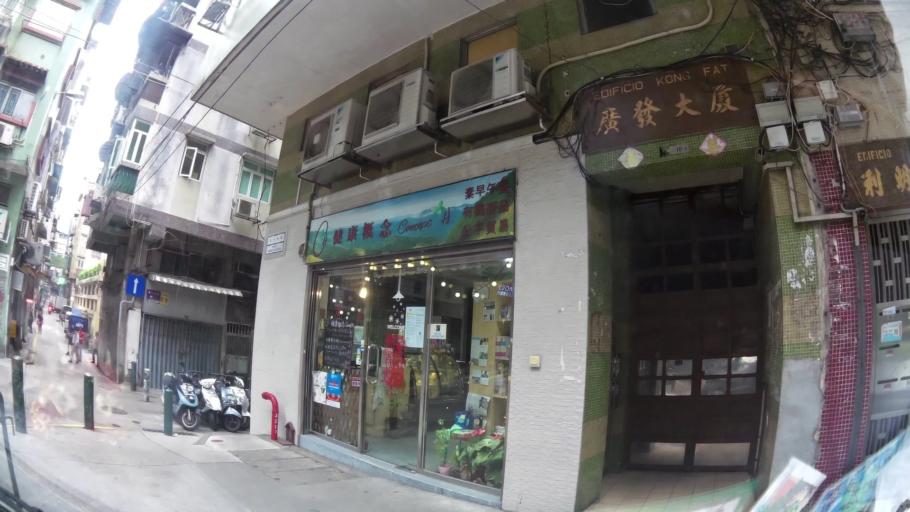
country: MO
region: Macau
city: Macau
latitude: 22.1956
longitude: 113.5454
